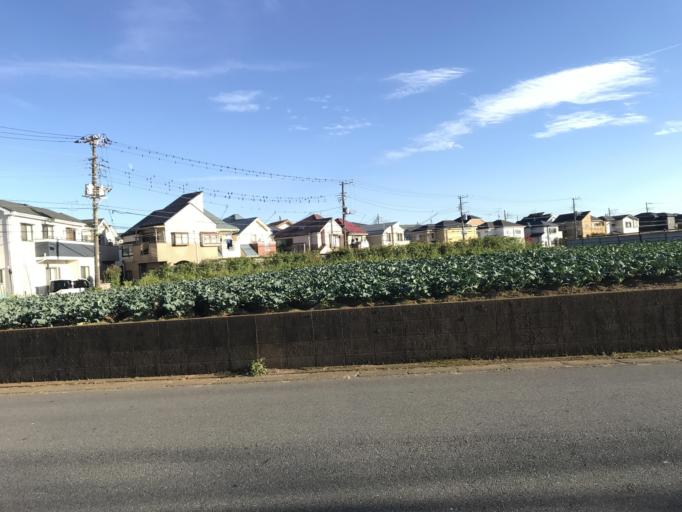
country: JP
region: Kanagawa
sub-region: Kawasaki-shi
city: Kawasaki
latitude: 35.5623
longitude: 139.6256
